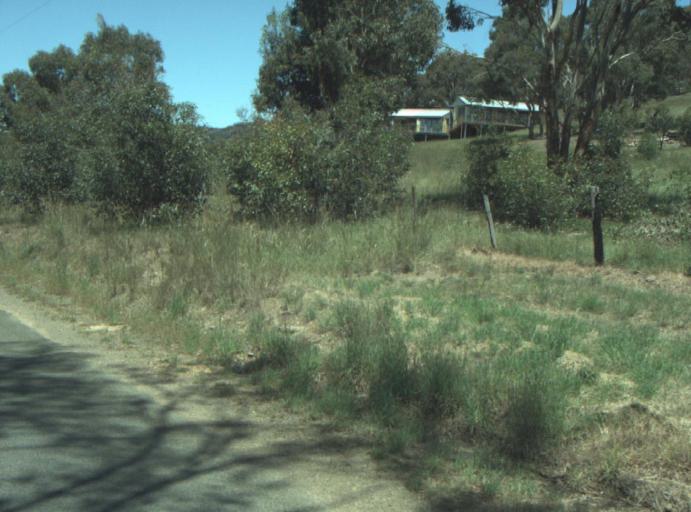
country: AU
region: Victoria
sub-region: Greater Geelong
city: Lara
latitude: -37.8405
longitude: 144.2834
